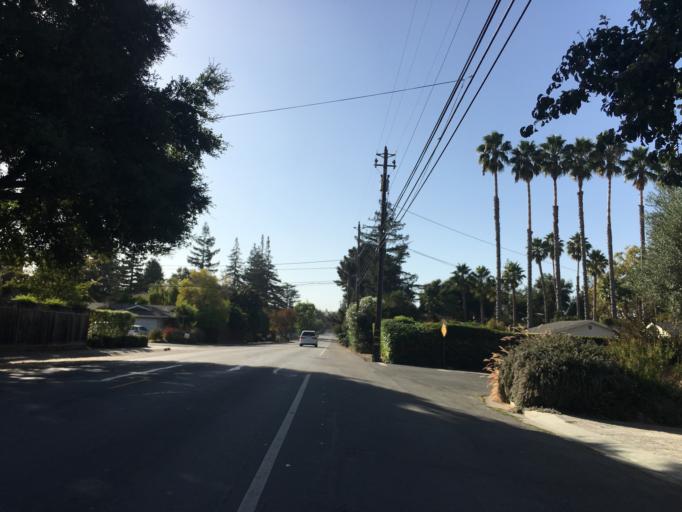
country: US
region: California
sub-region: Santa Clara County
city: Loyola
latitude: 37.3651
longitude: -122.0881
